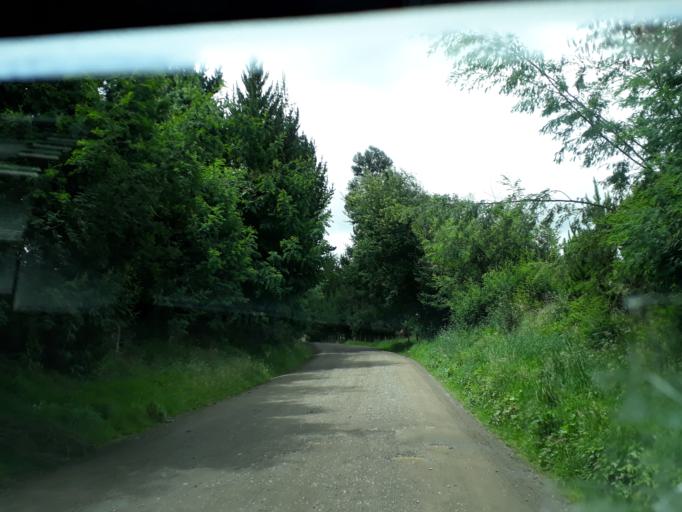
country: CO
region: Cundinamarca
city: La Mesa
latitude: 5.2040
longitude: -73.9212
